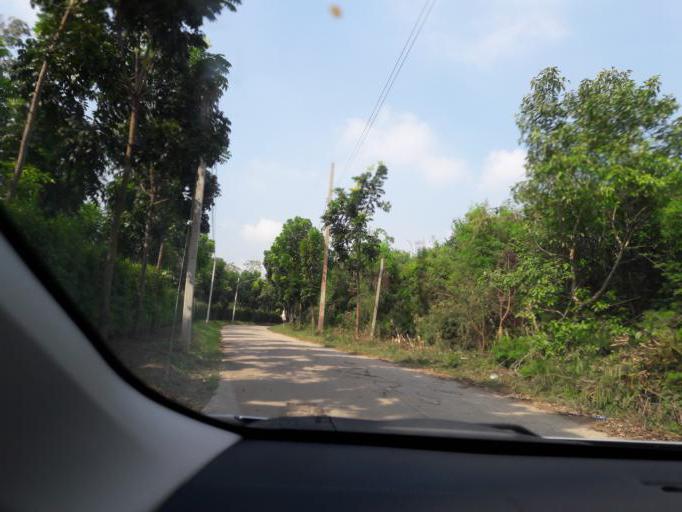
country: TH
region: Ang Thong
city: Ang Thong
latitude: 14.5501
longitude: 100.4370
